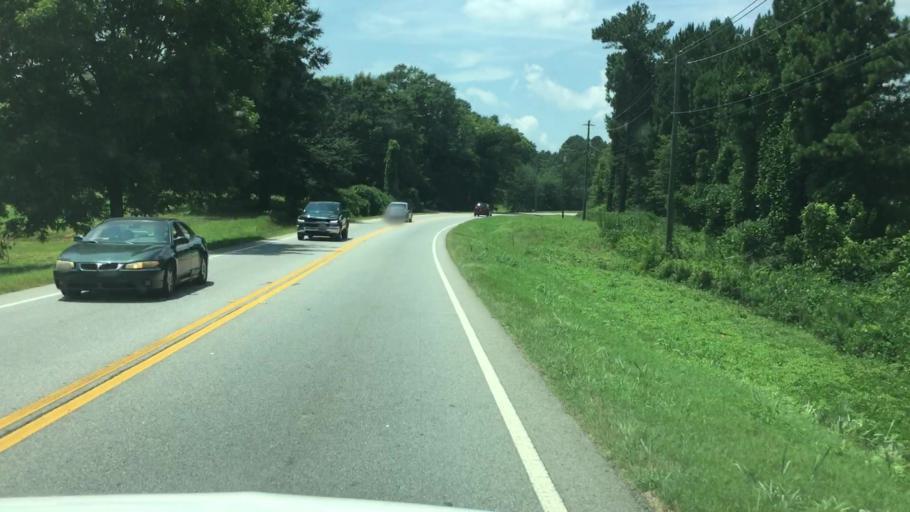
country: US
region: Georgia
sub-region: Barrow County
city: Auburn
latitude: 33.9919
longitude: -83.7798
